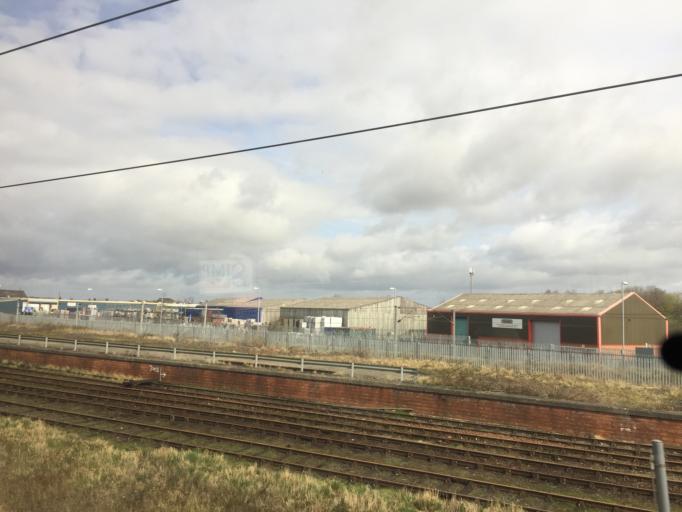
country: GB
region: England
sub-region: Cumbria
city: Carlisle
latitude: 54.8837
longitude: -2.9241
